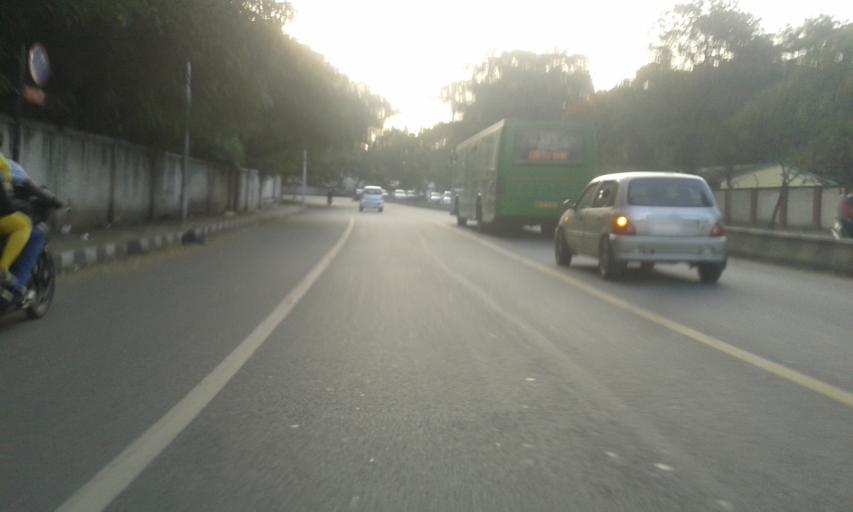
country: IN
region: Karnataka
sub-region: Bangalore Urban
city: Bangalore
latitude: 12.9616
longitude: 77.6339
